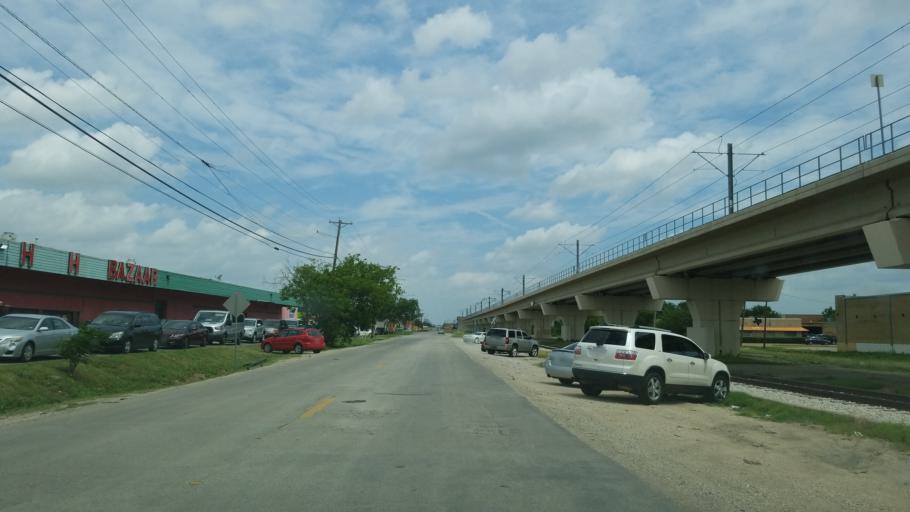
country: US
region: Texas
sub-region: Dallas County
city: Farmers Branch
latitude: 32.8731
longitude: -96.8814
